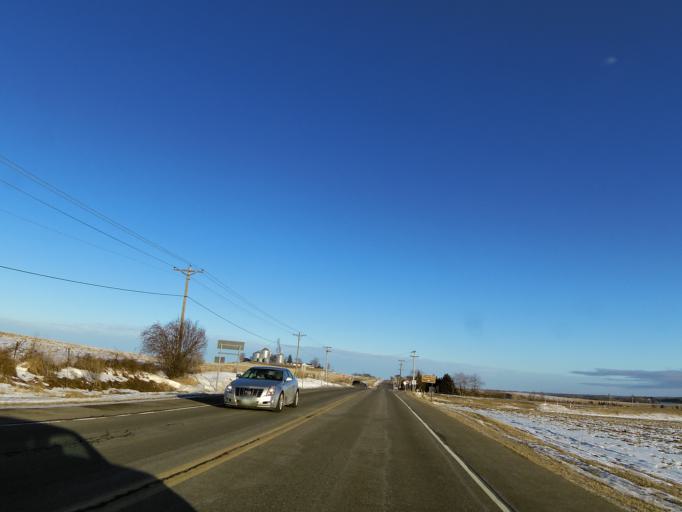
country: US
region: Minnesota
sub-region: Washington County
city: Cottage Grove
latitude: 44.8480
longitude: -92.8647
